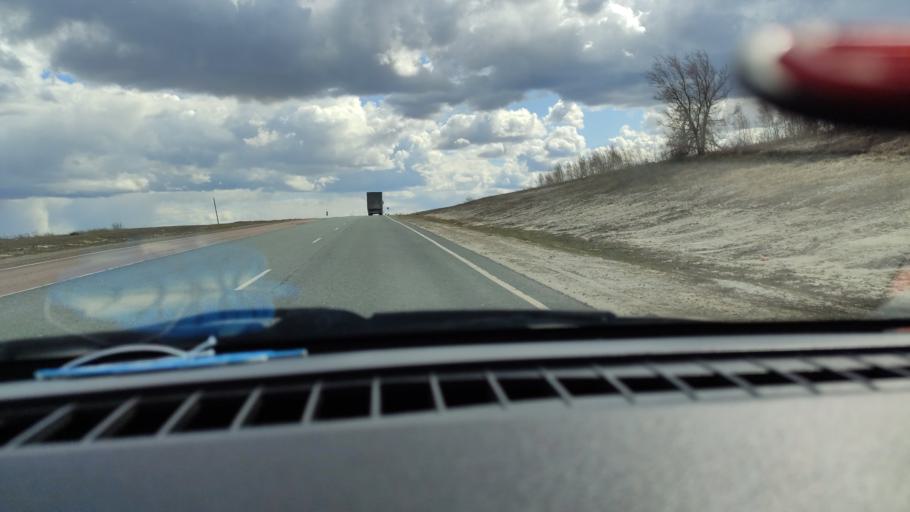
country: RU
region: Samara
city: Syzran'
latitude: 52.9552
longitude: 48.3076
